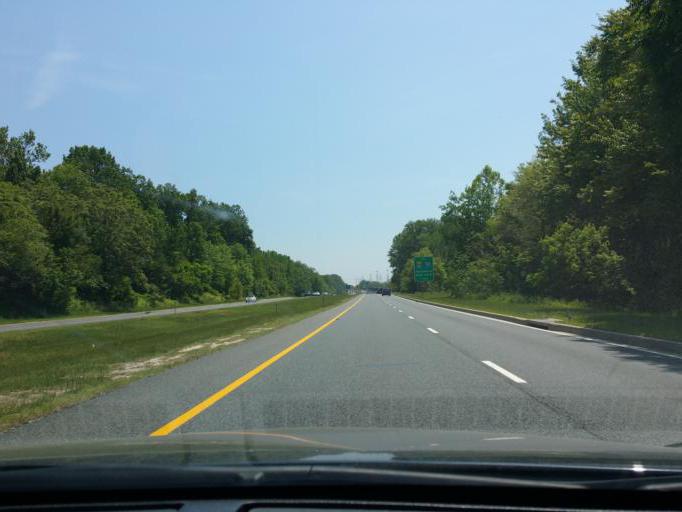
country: US
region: Maryland
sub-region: Baltimore County
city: Perry Hall
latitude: 39.3800
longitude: -76.4782
